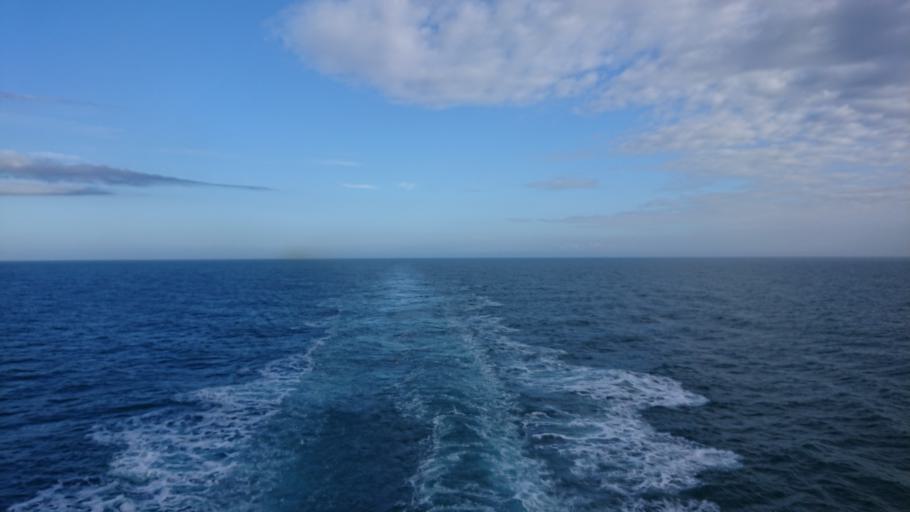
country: GB
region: Wales
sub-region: Pembrokeshire
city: Saint David's
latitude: 52.1339
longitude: -5.6122
